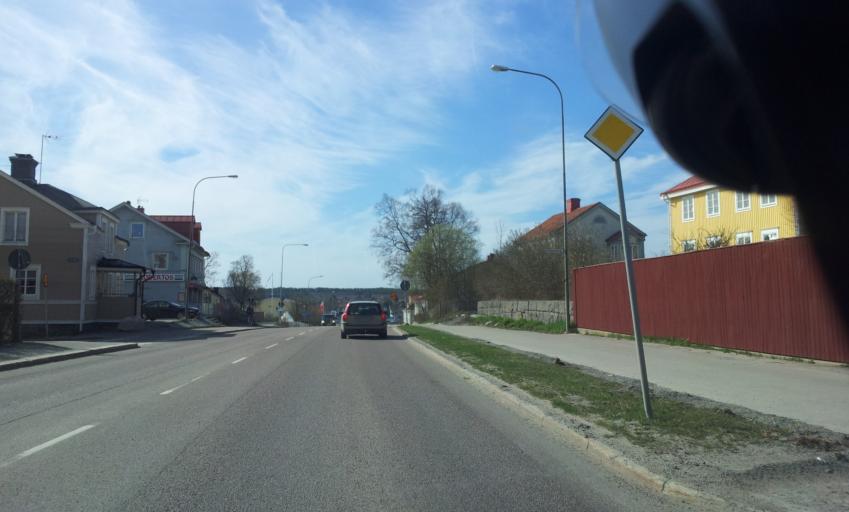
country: SE
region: Gaevleborg
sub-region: Hudiksvalls Kommun
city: Hudiksvall
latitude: 61.7220
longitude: 17.1002
